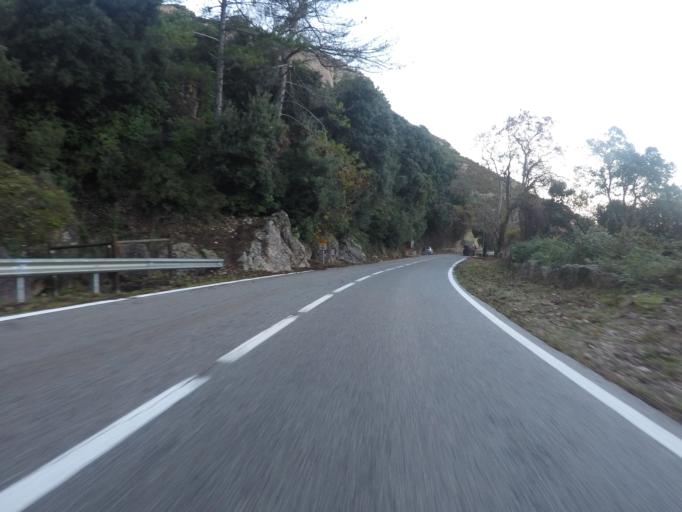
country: ES
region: Catalonia
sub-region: Provincia de Barcelona
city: Monistrol de Montserrat
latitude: 41.6090
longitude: 1.8217
